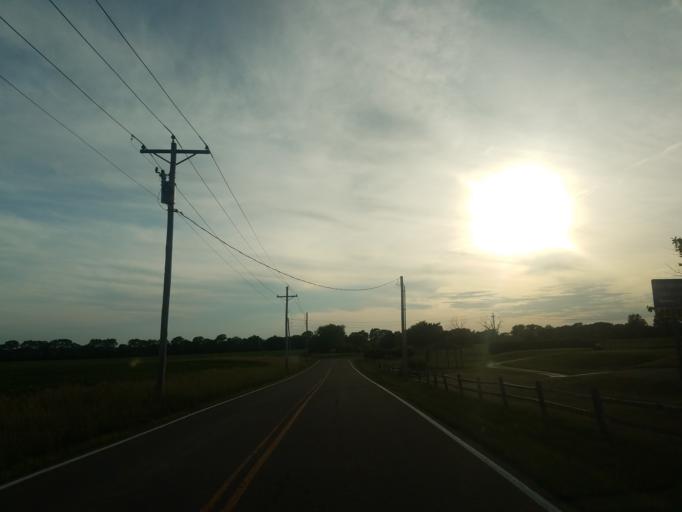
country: US
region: Illinois
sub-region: McLean County
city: Bloomington
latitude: 40.4416
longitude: -89.0039
